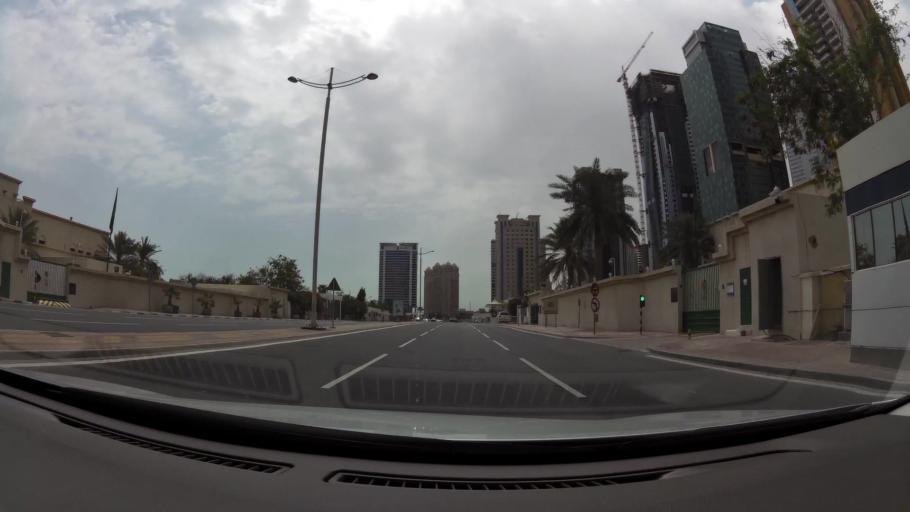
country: QA
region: Baladiyat ad Dawhah
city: Doha
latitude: 25.3305
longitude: 51.5367
